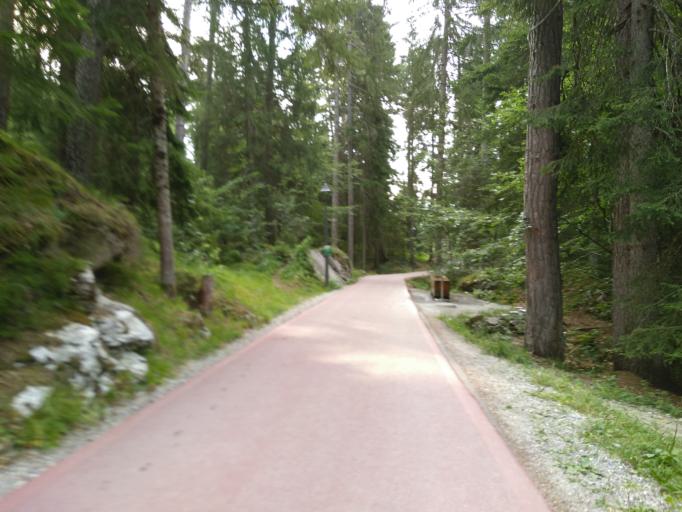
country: CH
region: Grisons
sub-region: Imboden District
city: Flims
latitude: 46.8234
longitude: 9.2937
